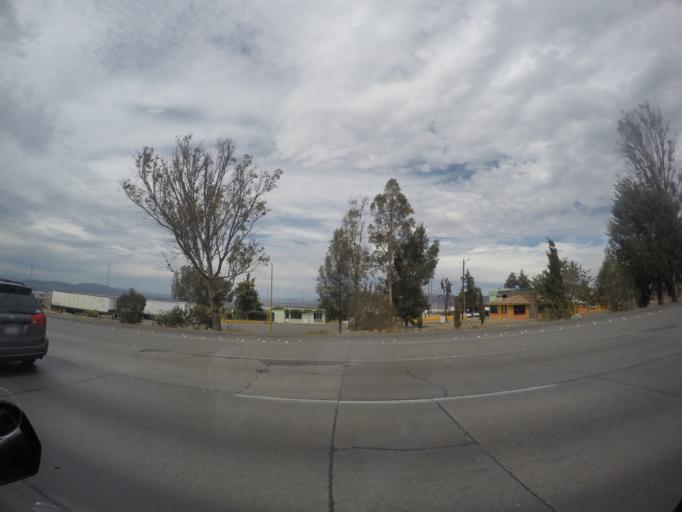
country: MX
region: Queretaro
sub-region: San Juan del Rio
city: Paso de Mata
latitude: 20.3594
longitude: -99.9625
